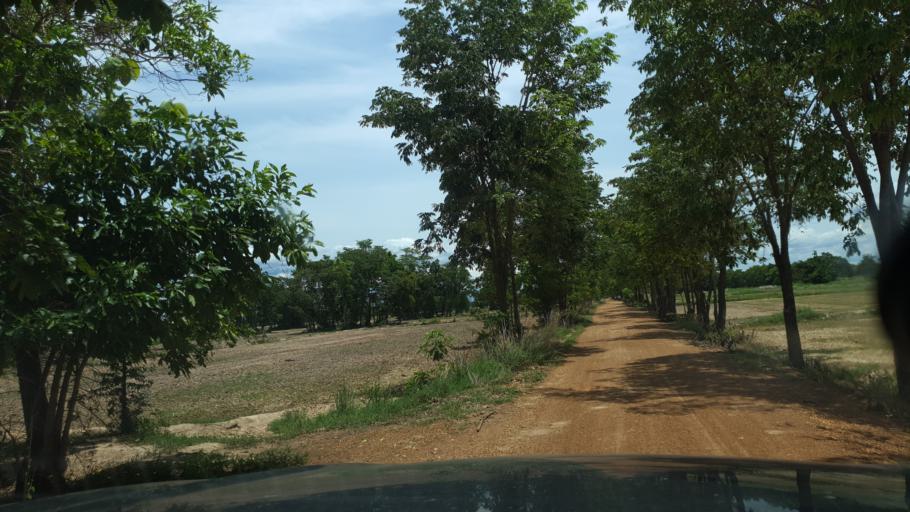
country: TH
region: Sukhothai
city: Ban Na
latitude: 17.1393
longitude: 99.6695
